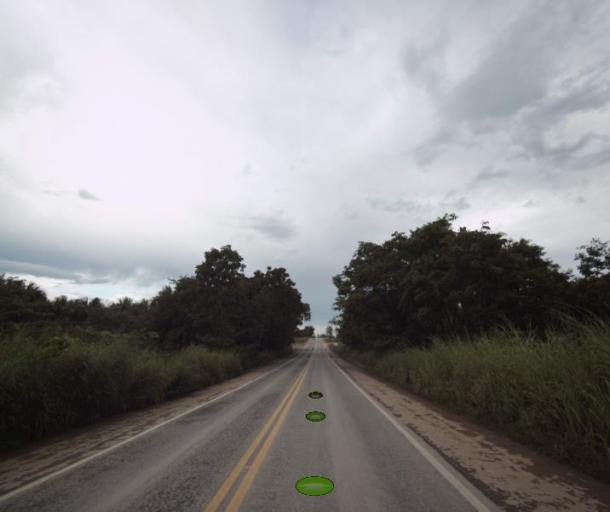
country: BR
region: Goias
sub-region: Porangatu
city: Porangatu
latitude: -13.5949
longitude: -49.0418
